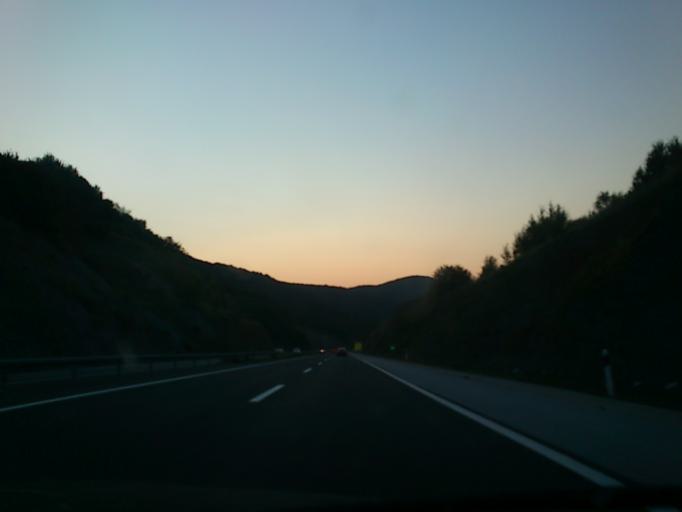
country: HR
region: Karlovacka
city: Ostarije
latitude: 45.1801
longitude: 15.2746
